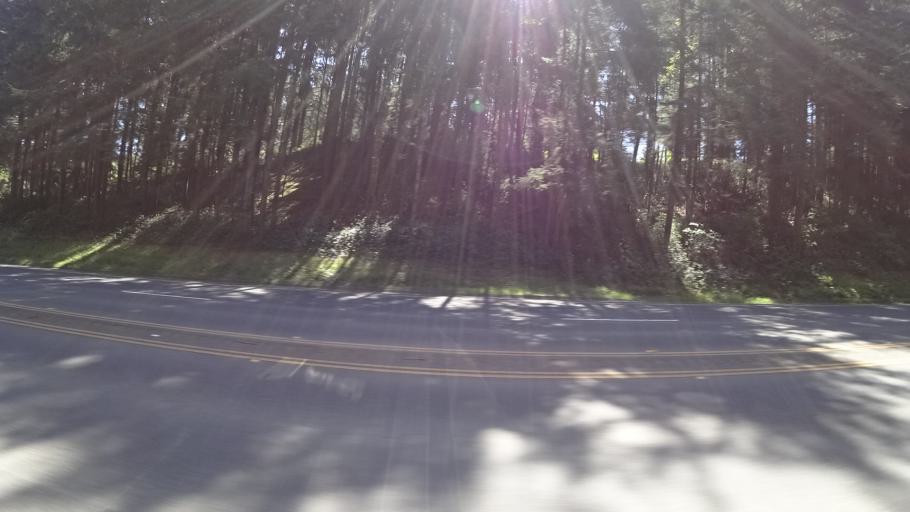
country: US
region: California
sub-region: Humboldt County
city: Westhaven-Moonstone
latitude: 41.1528
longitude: -124.1324
